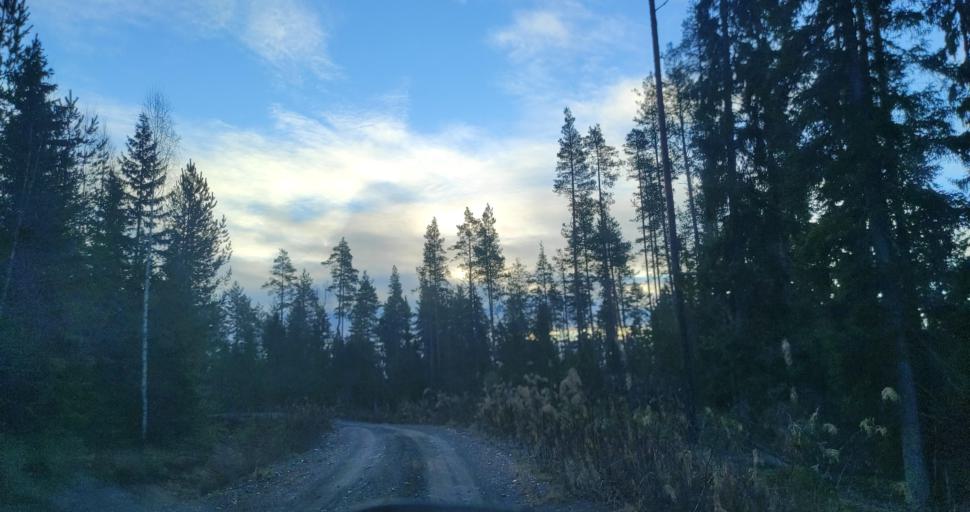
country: RU
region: Republic of Karelia
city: Pitkyaranta
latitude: 61.7406
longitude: 31.3618
